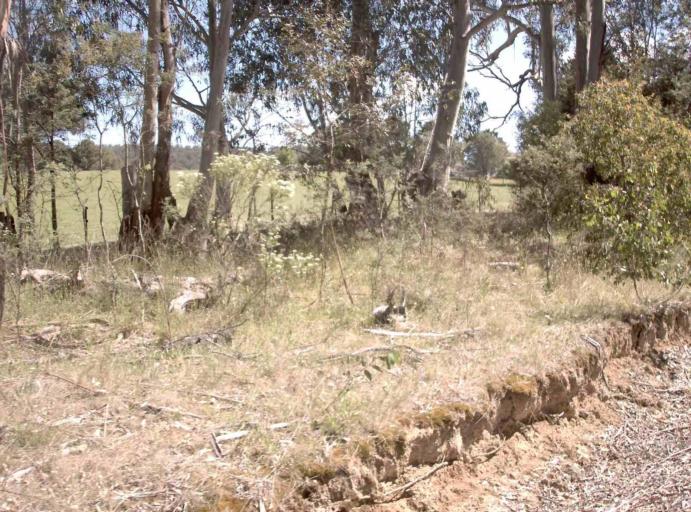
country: AU
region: New South Wales
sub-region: Bombala
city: Bombala
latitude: -37.0577
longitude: 148.8031
